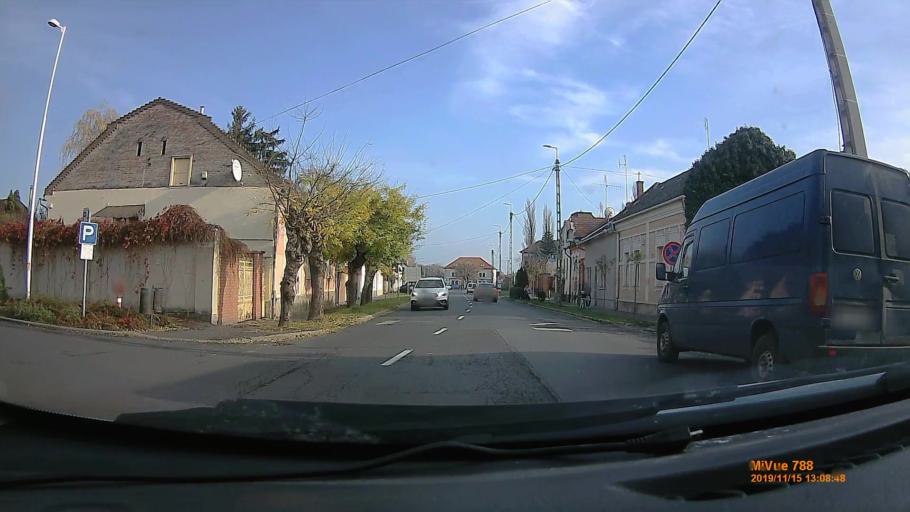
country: HU
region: Bekes
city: Gyula
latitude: 46.6434
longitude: 21.2737
